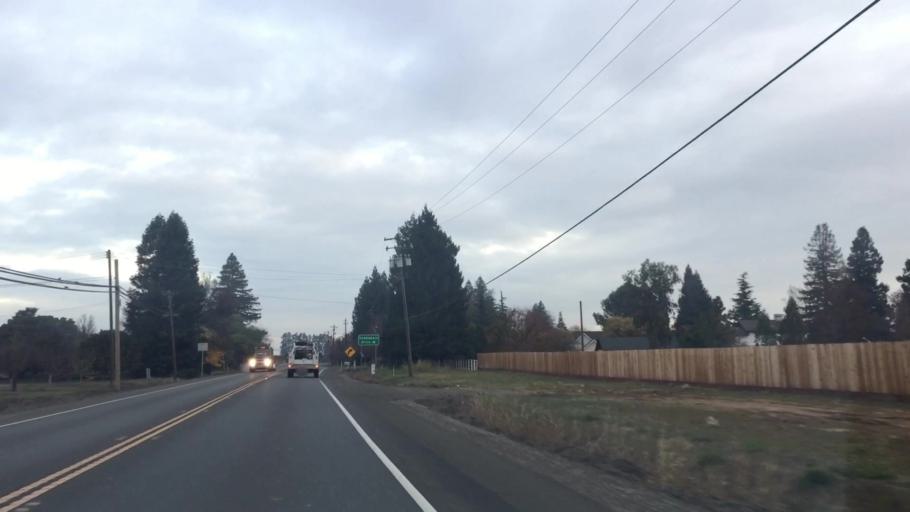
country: US
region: California
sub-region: Yuba County
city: Marysville
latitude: 39.1879
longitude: -121.5940
